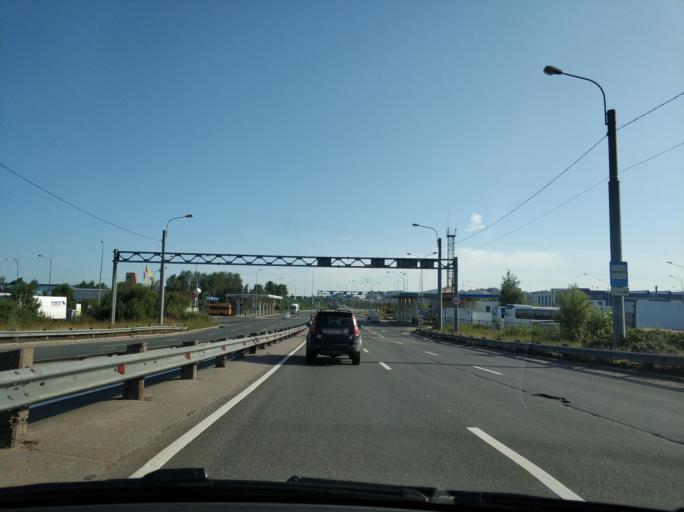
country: RU
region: Leningrad
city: Bugry
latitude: 60.0552
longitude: 30.3839
